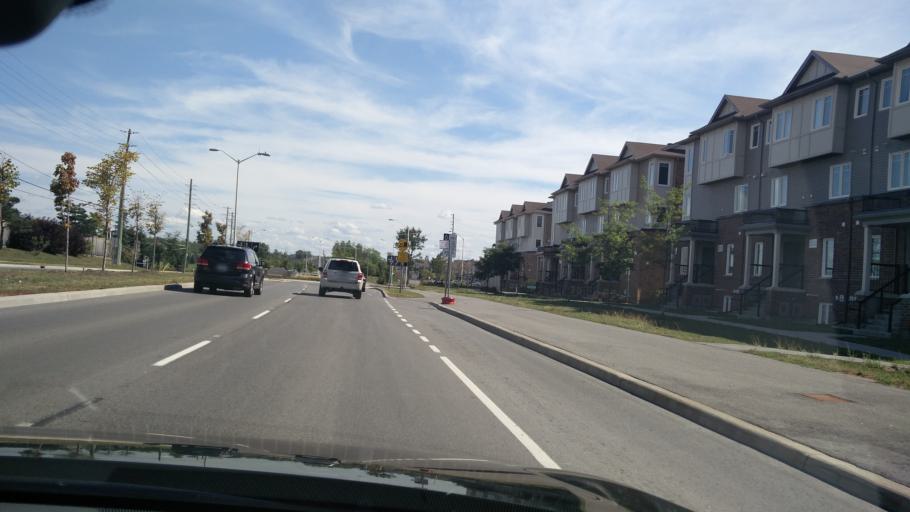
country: CA
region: Ontario
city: Bells Corners
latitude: 45.2575
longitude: -75.7294
